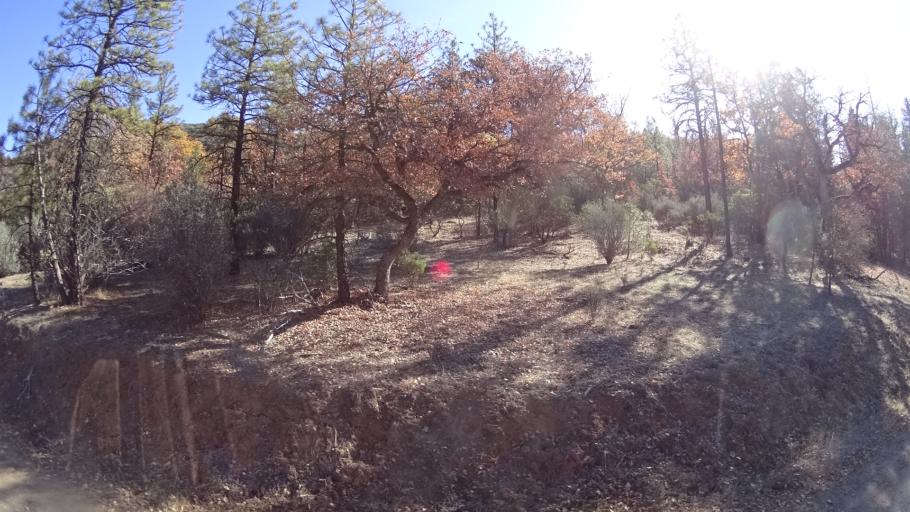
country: US
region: California
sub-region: Siskiyou County
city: Yreka
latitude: 41.8527
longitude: -122.8331
